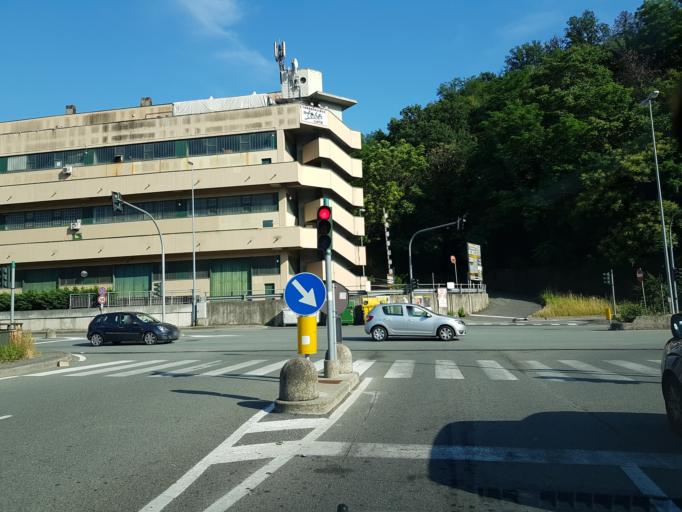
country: IT
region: Liguria
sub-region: Provincia di Genova
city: Piccarello
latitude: 44.4475
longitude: 9.0068
